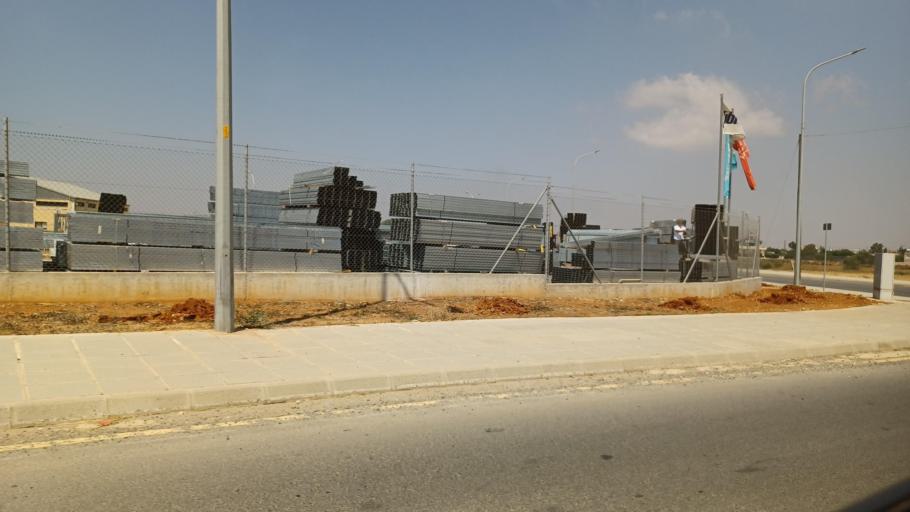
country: CY
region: Ammochostos
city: Deryneia
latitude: 35.0538
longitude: 33.9647
